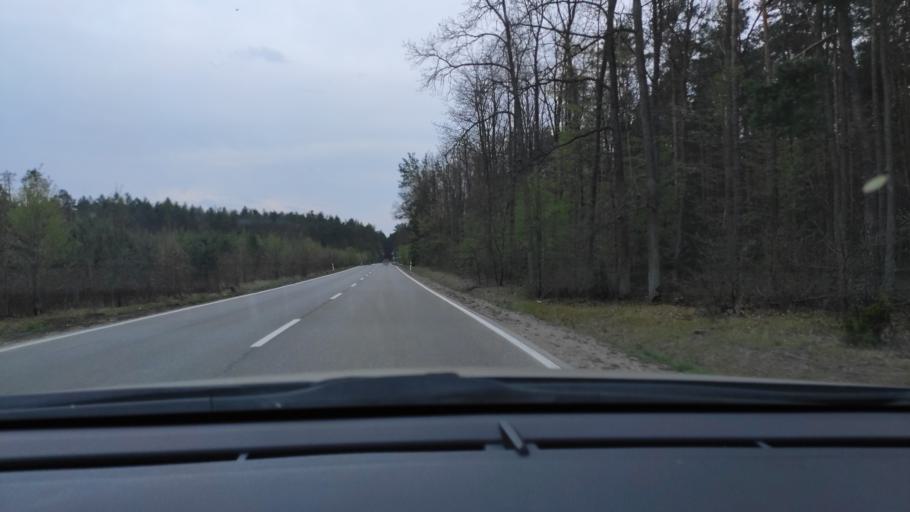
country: PL
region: Masovian Voivodeship
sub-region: Powiat radomski
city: Pionki
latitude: 51.4965
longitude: 21.4254
